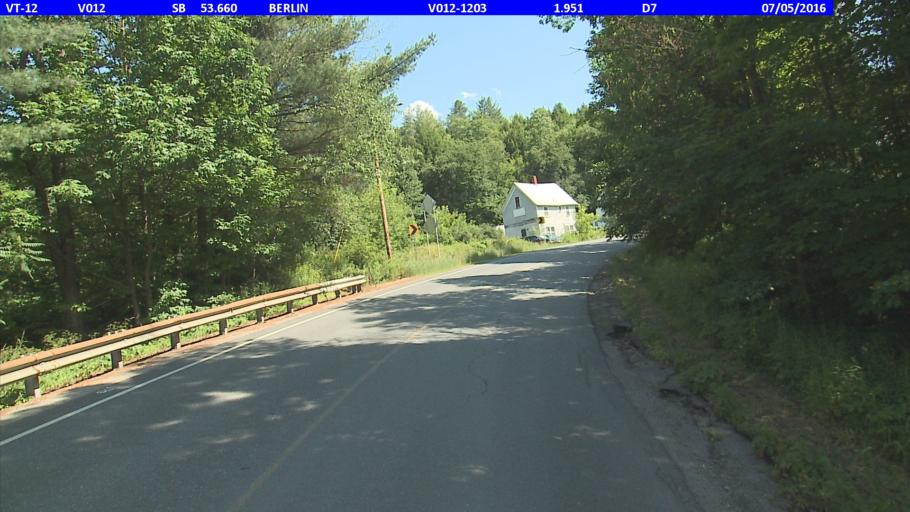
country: US
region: Vermont
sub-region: Washington County
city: Northfield
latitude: 44.1992
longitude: -72.6320
